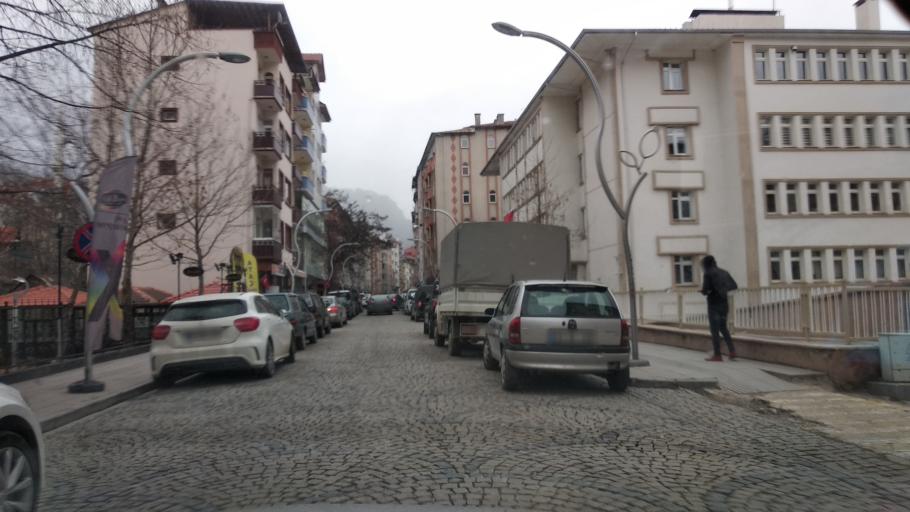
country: TR
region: Gumushane
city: Gumushkhane
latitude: 40.4616
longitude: 39.4716
